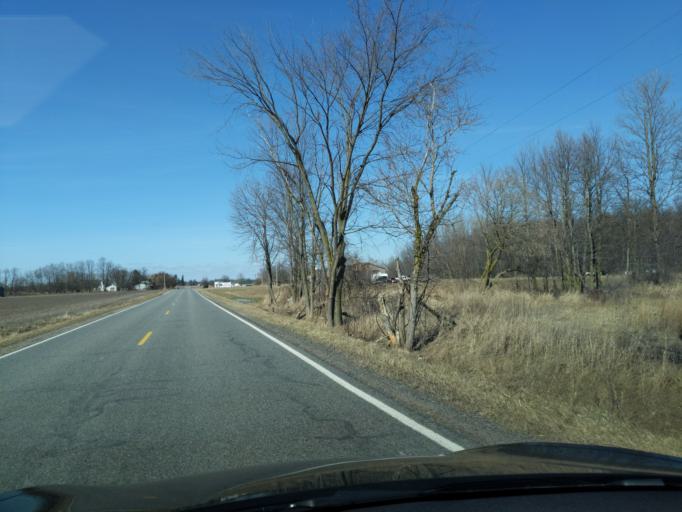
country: US
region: Michigan
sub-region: Ionia County
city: Saranac
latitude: 42.9048
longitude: -85.1341
